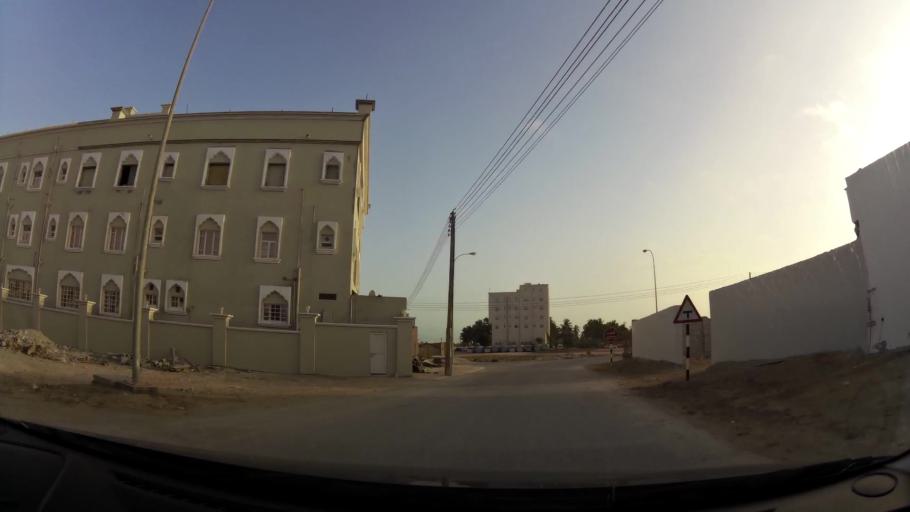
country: OM
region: Zufar
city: Salalah
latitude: 16.9999
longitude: 54.0337
